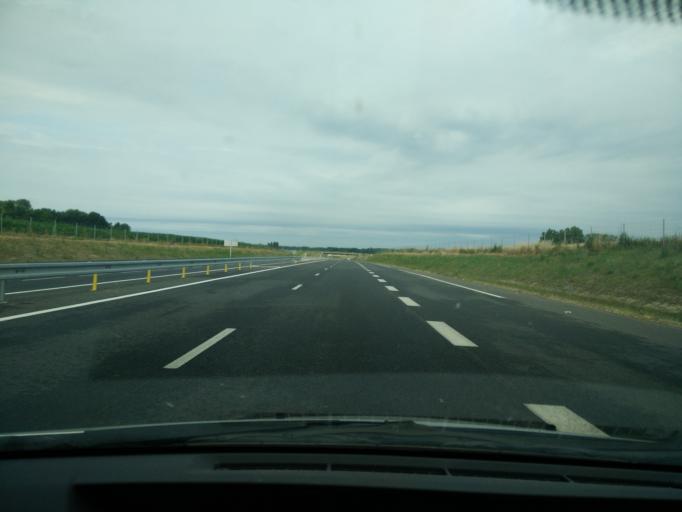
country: FR
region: Pays de la Loire
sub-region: Departement de Maine-et-Loire
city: Saint-Jean
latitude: 47.2876
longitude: -0.3769
